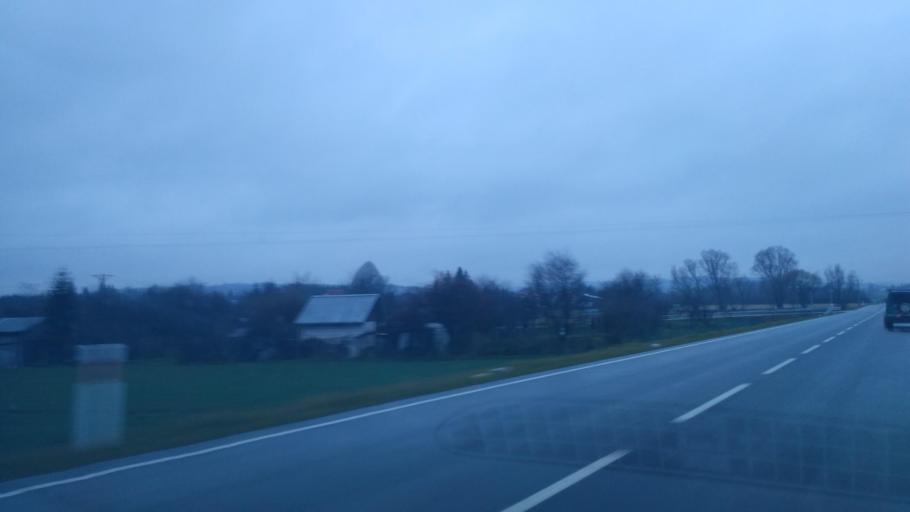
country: PL
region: Subcarpathian Voivodeship
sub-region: Powiat rzeszowski
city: Dynow
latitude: 49.8221
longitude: 22.2411
